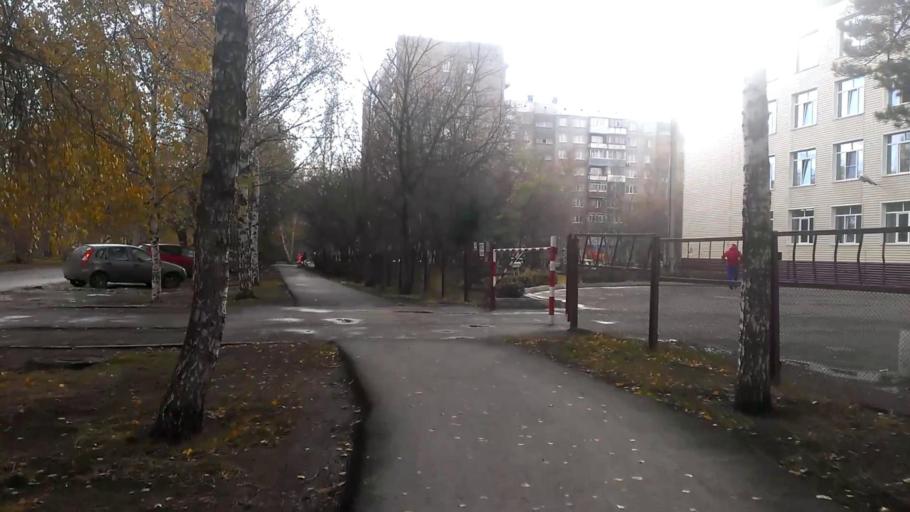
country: RU
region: Altai Krai
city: Novosilikatnyy
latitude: 53.3575
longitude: 83.6782
